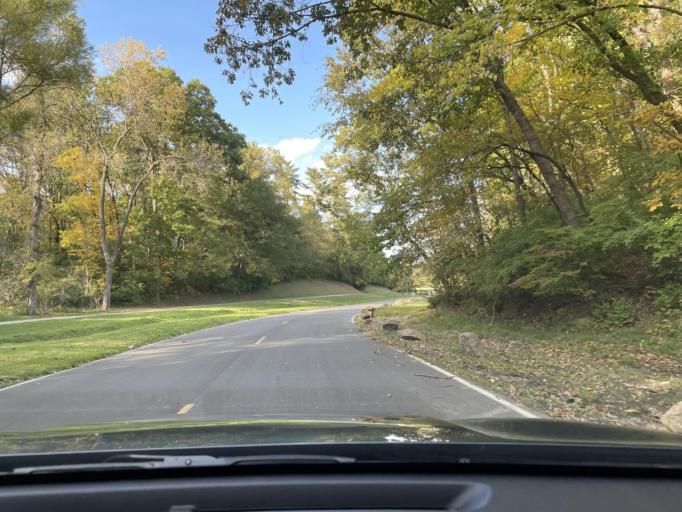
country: US
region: Kansas
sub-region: Doniphan County
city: Elwood
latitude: 39.7238
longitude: -94.8448
